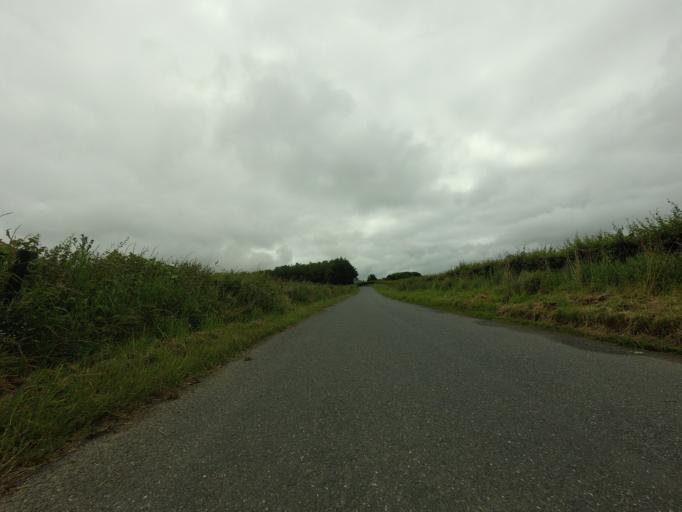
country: GB
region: Scotland
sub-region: Aberdeenshire
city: Rosehearty
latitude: 57.5401
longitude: -2.1918
